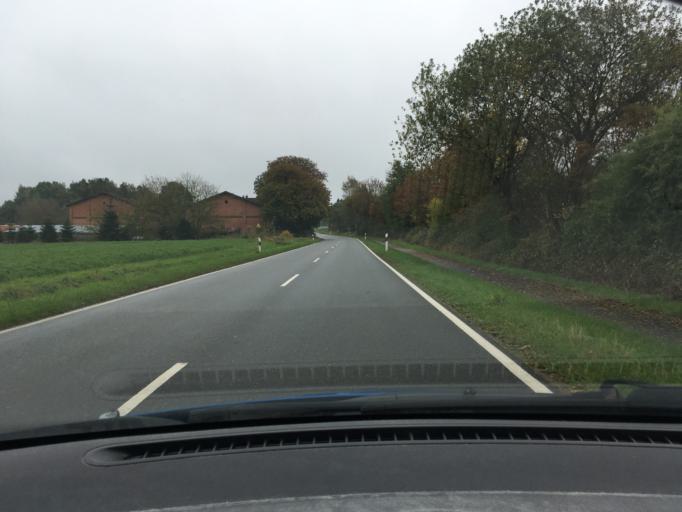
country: DE
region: Schleswig-Holstein
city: Bosdorf
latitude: 54.1127
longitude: 10.4782
